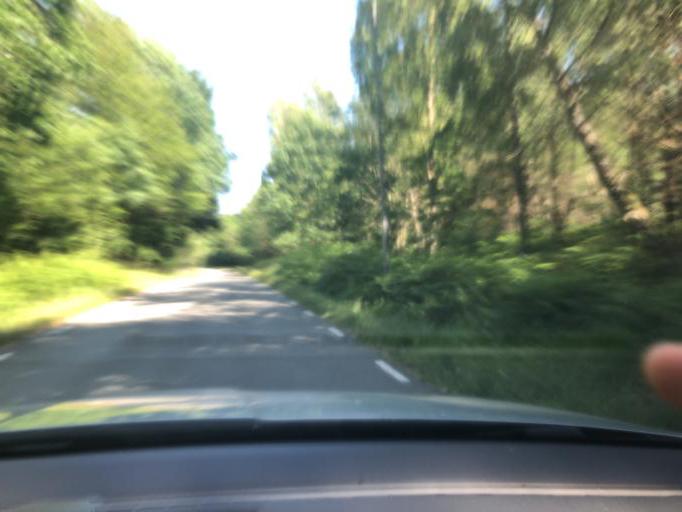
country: SE
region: Blekinge
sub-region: Karlshamns Kommun
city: Morrum
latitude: 56.1715
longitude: 14.6507
